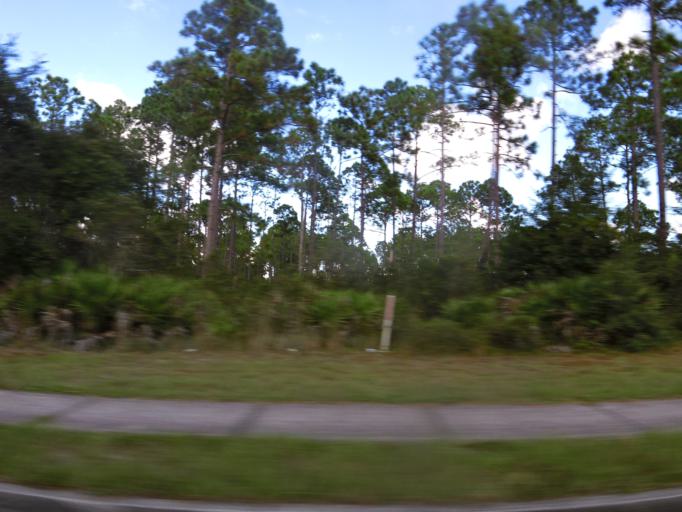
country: US
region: Florida
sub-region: Duval County
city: Jacksonville Beach
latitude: 30.2781
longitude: -81.4404
